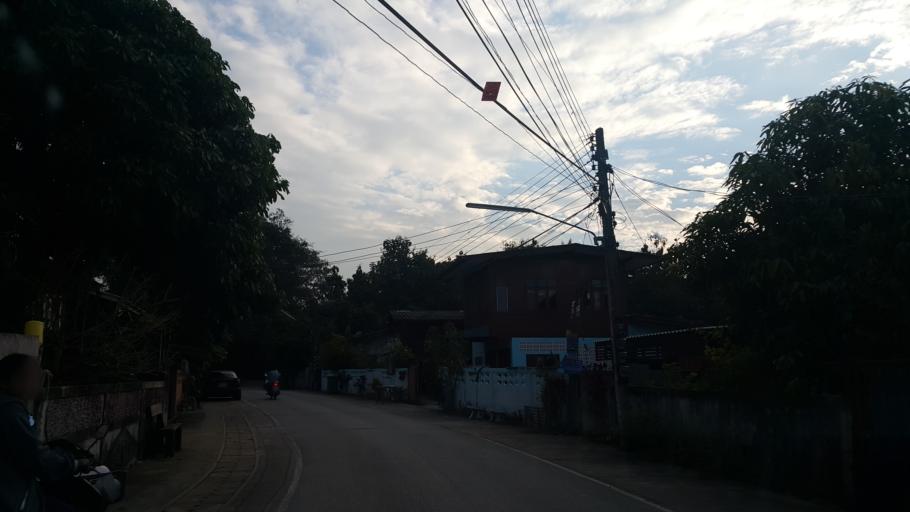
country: TH
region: Lampang
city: Sop Prap
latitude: 17.8726
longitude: 99.3324
